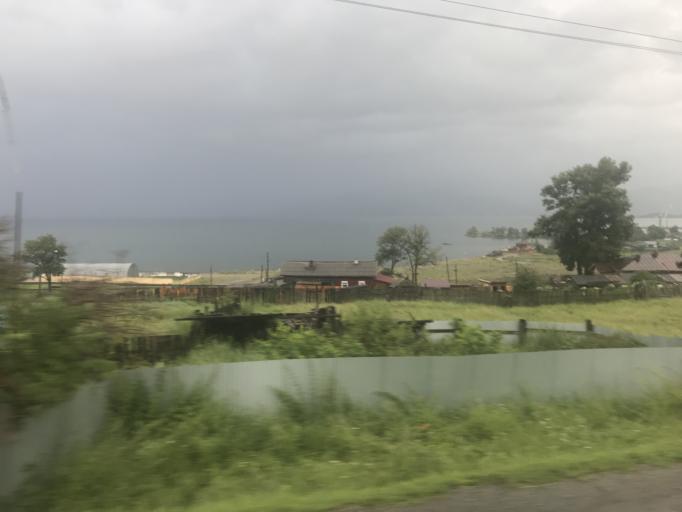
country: RU
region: Irkutsk
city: Kultuk
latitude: 51.7301
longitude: 103.7188
